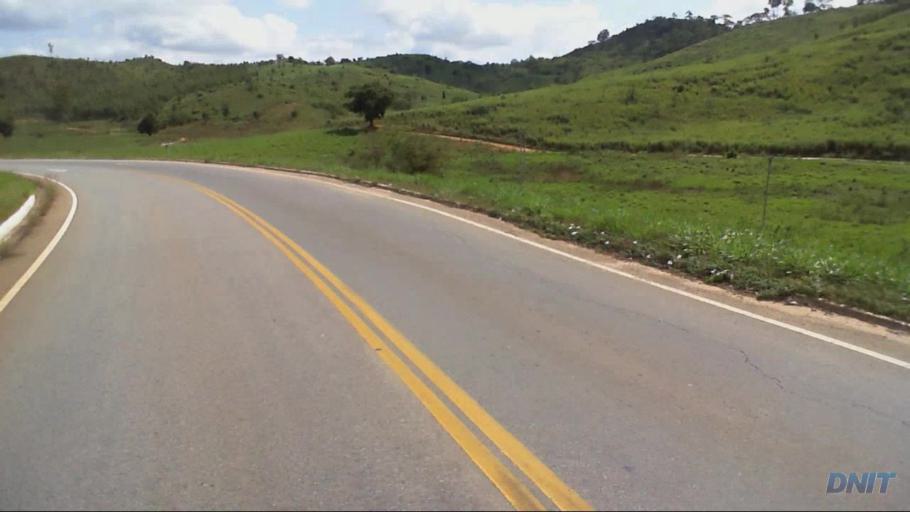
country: BR
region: Minas Gerais
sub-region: Governador Valadares
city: Governador Valadares
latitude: -18.9129
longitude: -42.0095
